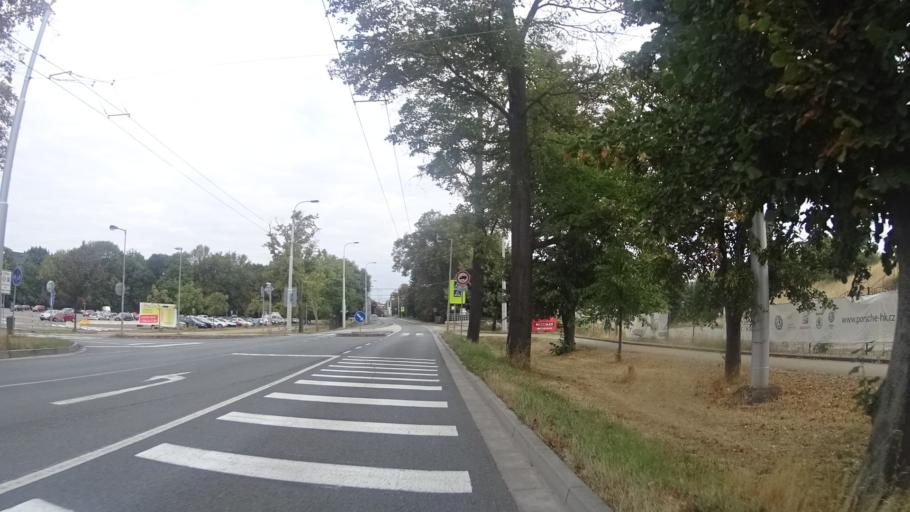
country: CZ
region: Kralovehradecky
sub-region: Okres Hradec Kralove
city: Hradec Kralove
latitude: 50.2057
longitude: 15.8439
